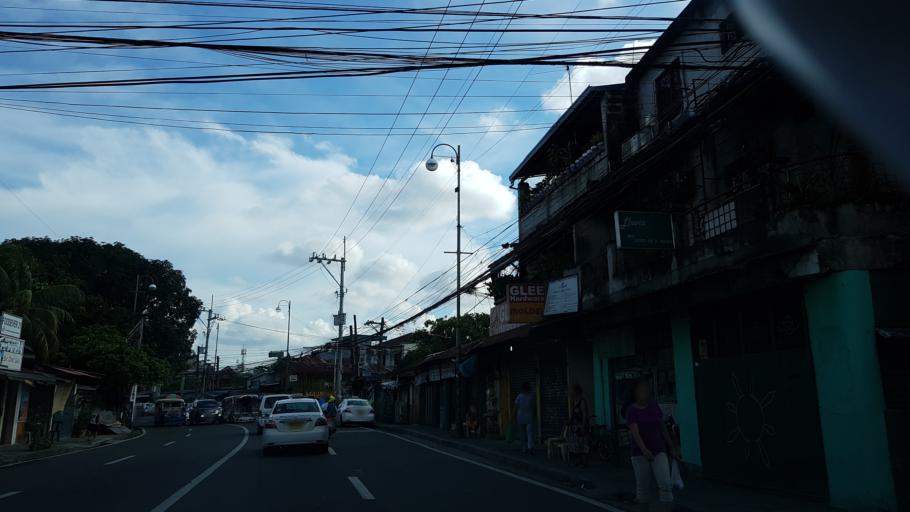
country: PH
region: Calabarzon
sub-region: Province of Rizal
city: Pateros
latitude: 14.5526
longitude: 121.0634
